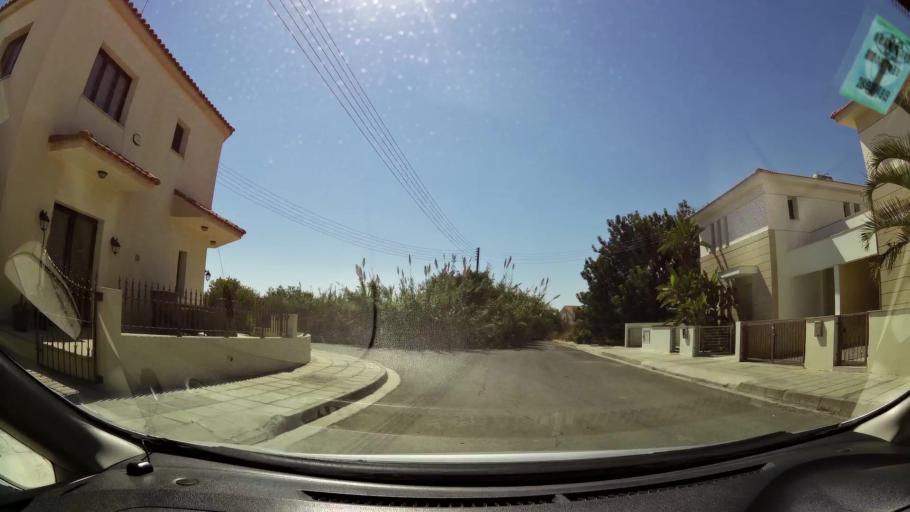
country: CY
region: Larnaka
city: Livadia
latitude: 34.9522
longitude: 33.6312
